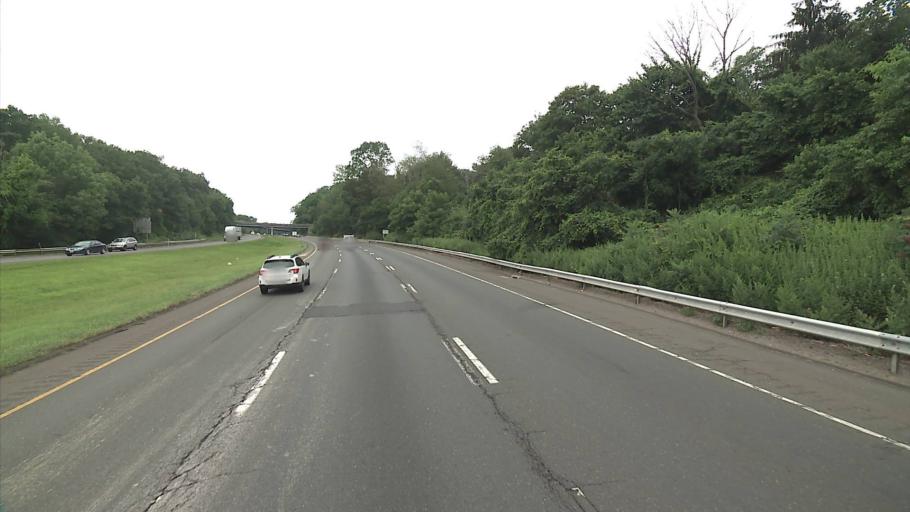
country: US
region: Connecticut
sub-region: Fairfield County
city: Newtown
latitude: 41.4293
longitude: -73.3176
